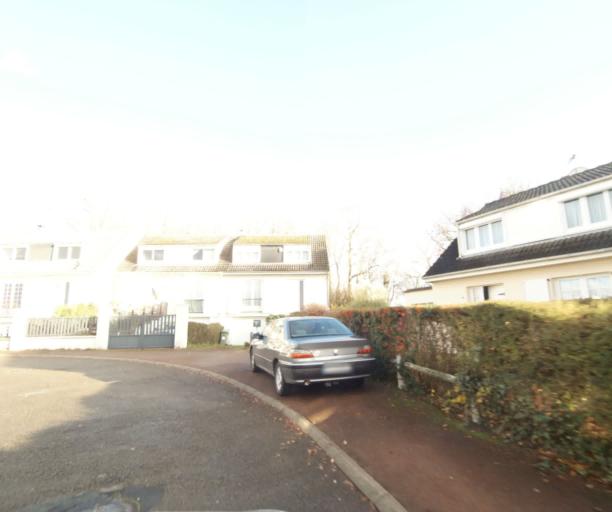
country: FR
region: Ile-de-France
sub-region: Departement des Yvelines
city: Meulan-en-Yvelines
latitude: 49.0102
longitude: 1.9225
